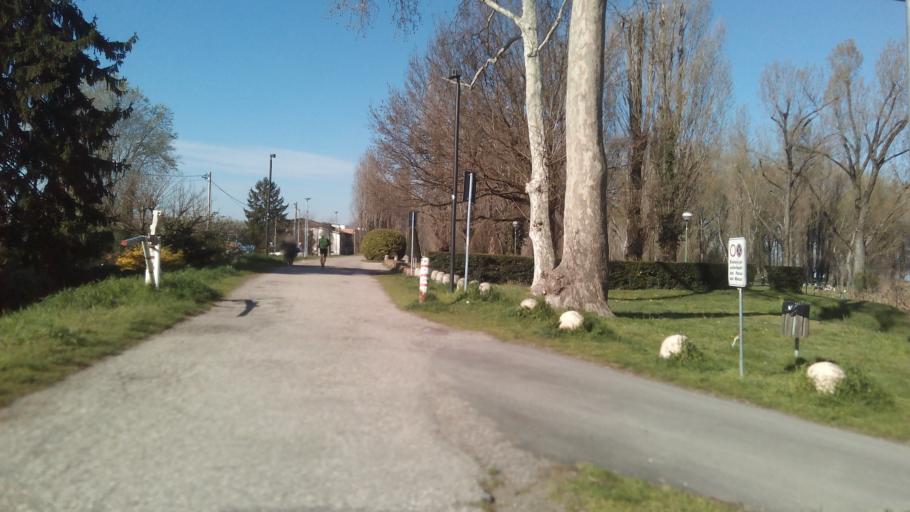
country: IT
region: Lombardy
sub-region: Provincia di Mantova
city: Mantova
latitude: 45.1569
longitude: 10.7771
